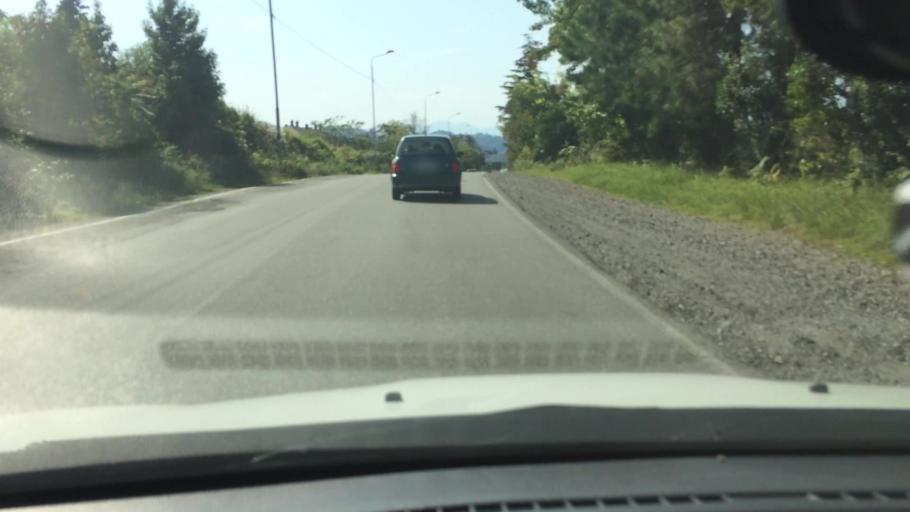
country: GE
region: Ajaria
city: Makhinjauri
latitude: 41.7385
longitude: 41.7354
